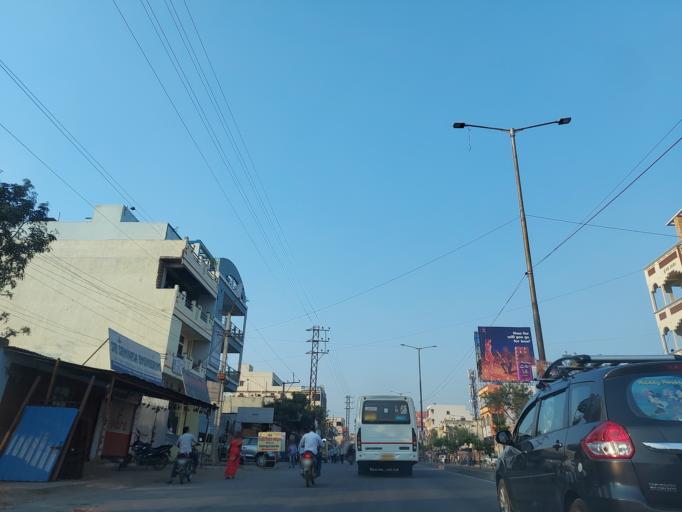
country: IN
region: Telangana
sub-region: Rangareddi
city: Balapur
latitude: 17.2061
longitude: 78.4764
